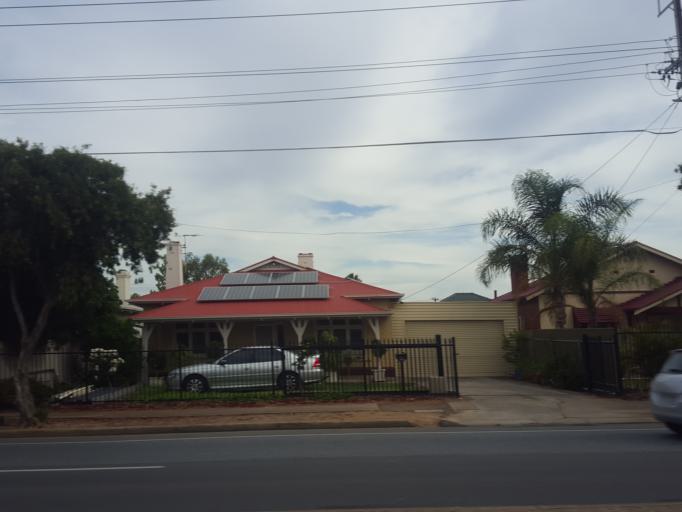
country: AU
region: South Australia
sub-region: Port Adelaide Enfield
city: Alberton
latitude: -34.8512
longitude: 138.5315
